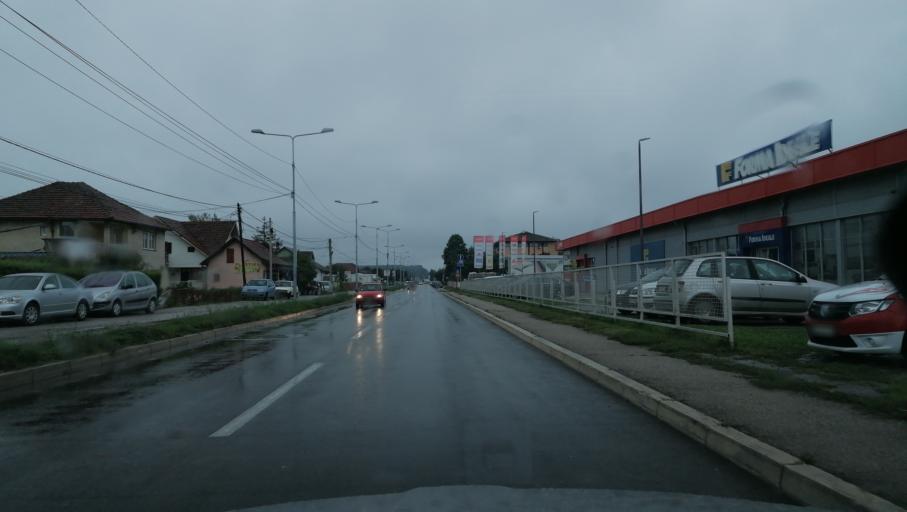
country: RS
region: Central Serbia
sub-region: Raski Okrug
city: Kraljevo
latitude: 43.7301
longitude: 20.6638
